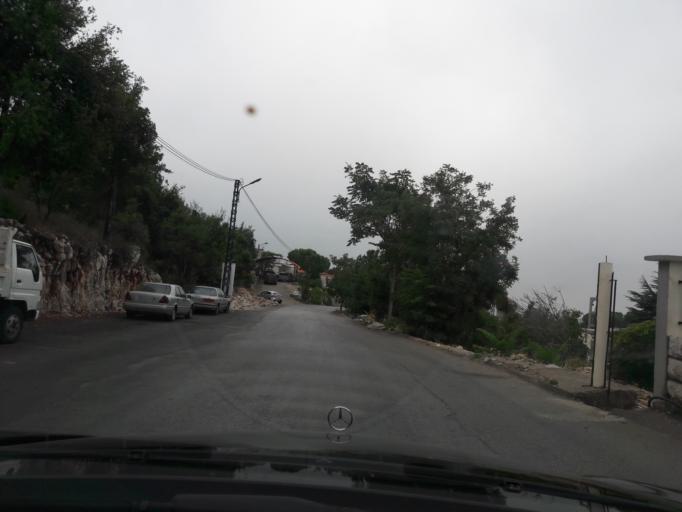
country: LB
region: Mont-Liban
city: Djounie
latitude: 33.9892
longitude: 35.6828
